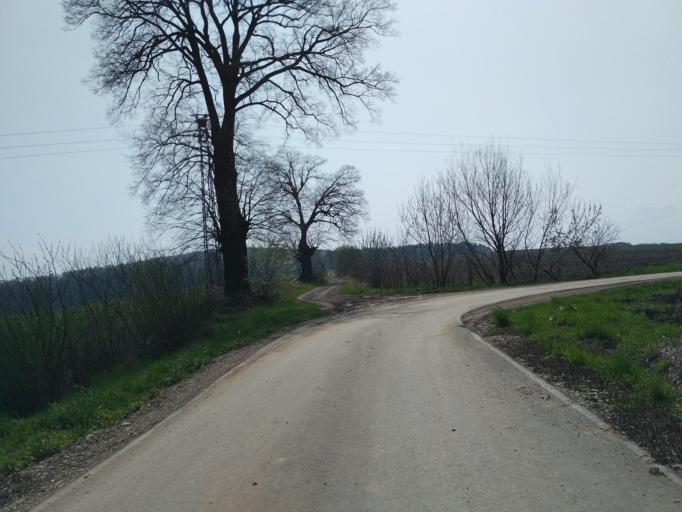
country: PL
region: Subcarpathian Voivodeship
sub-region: Powiat brzozowski
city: Turze Pole
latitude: 49.6401
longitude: 22.0049
